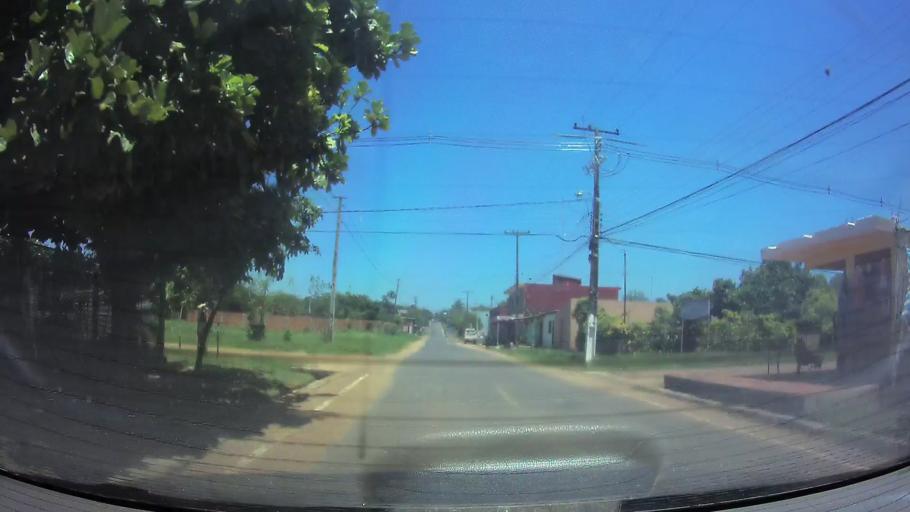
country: PY
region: Central
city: San Lorenzo
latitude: -25.3220
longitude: -57.4850
